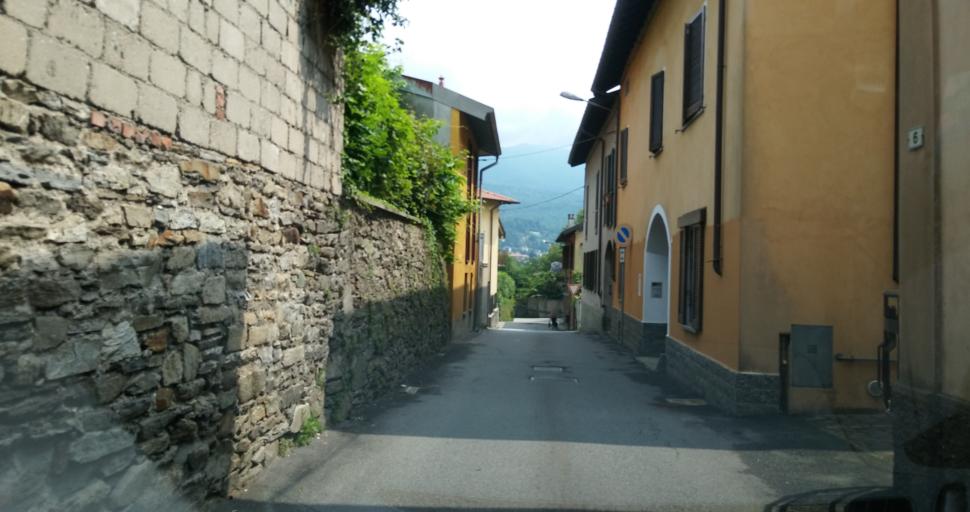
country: IT
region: Lombardy
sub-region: Provincia di Varese
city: Bardello
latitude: 45.8347
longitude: 8.6991
